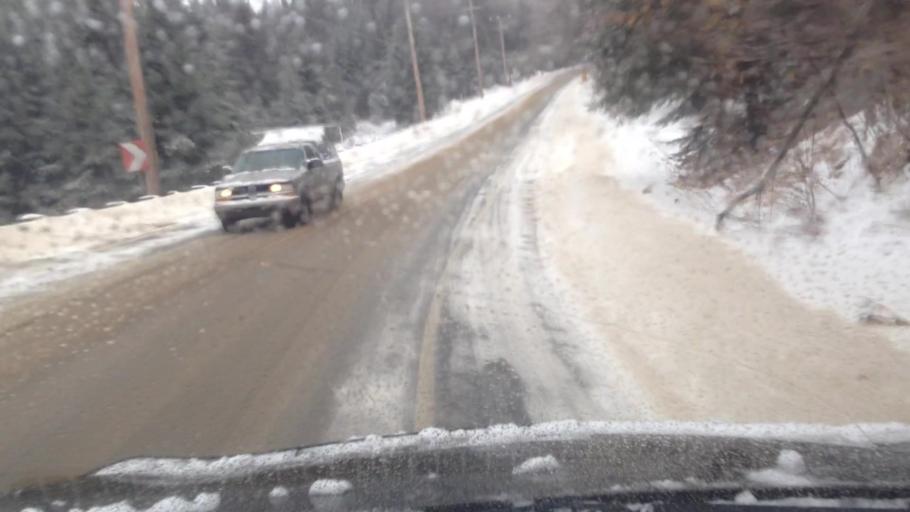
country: CA
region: Quebec
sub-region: Laurentides
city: Mont-Tremblant
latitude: 46.0240
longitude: -74.6066
